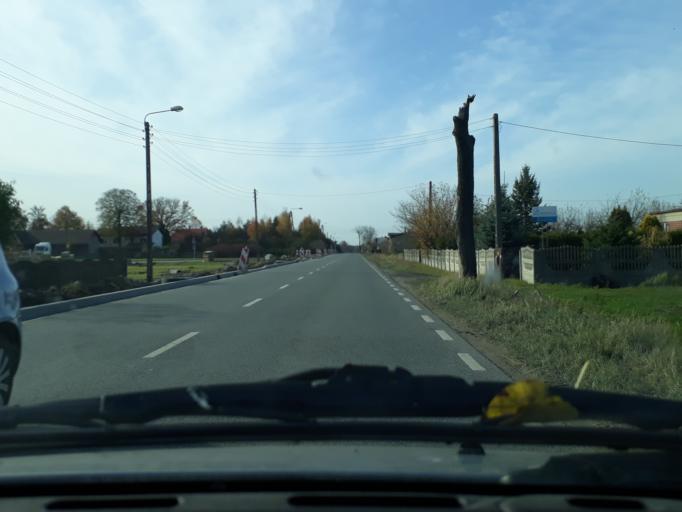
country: PL
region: Silesian Voivodeship
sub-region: Powiat lubliniecki
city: Psary
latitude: 50.5769
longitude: 18.9956
